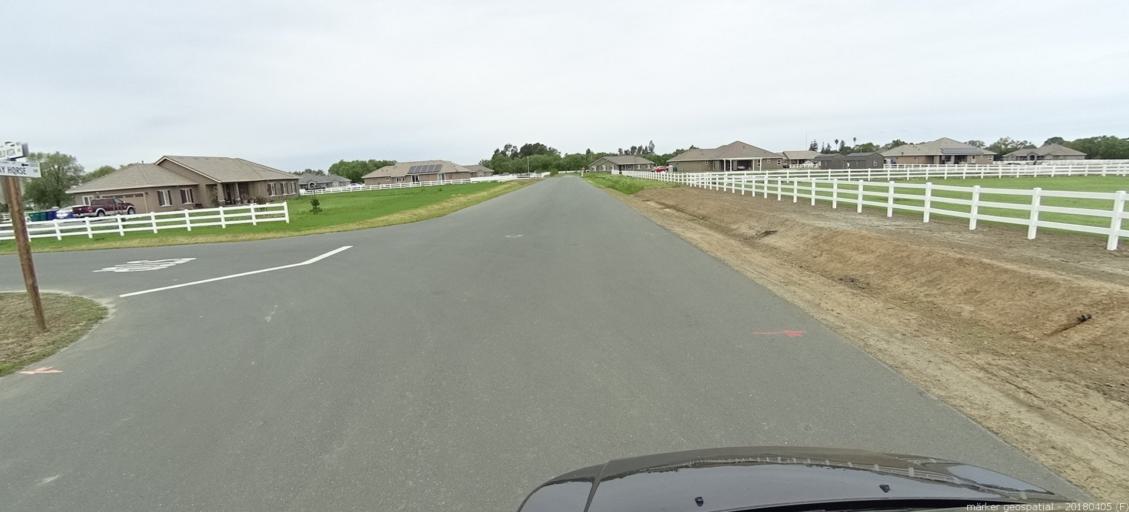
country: US
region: California
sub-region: Sacramento County
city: Galt
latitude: 38.2755
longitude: -121.3288
